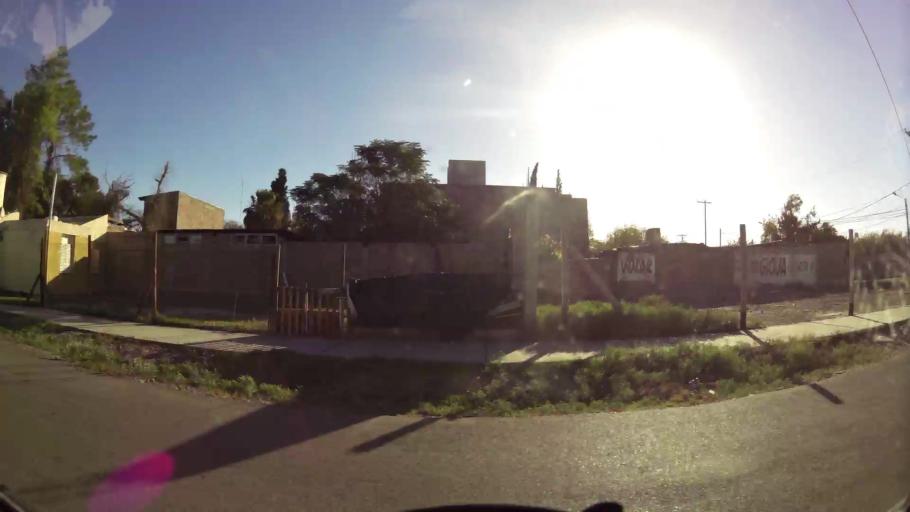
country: AR
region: San Juan
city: Villa Krause
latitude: -31.5594
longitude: -68.5181
